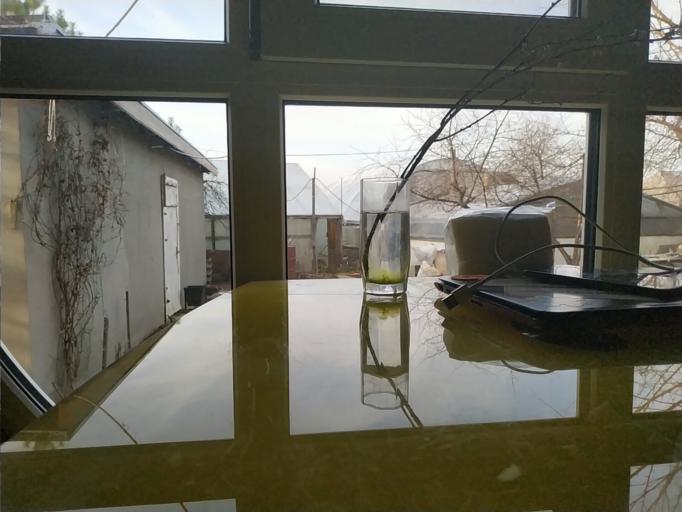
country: RU
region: Republic of Karelia
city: Suoyarvi
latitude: 62.0248
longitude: 32.1984
